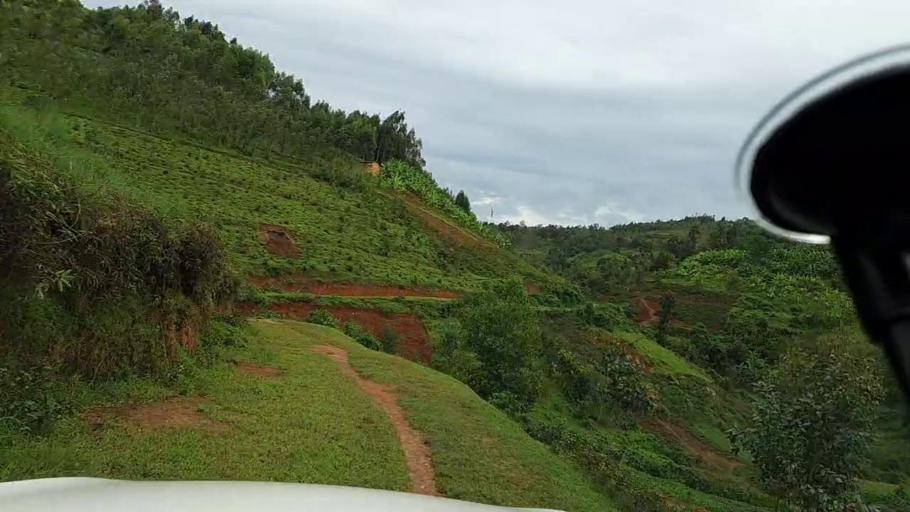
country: RW
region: Southern Province
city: Gitarama
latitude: -2.0816
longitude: 29.6451
